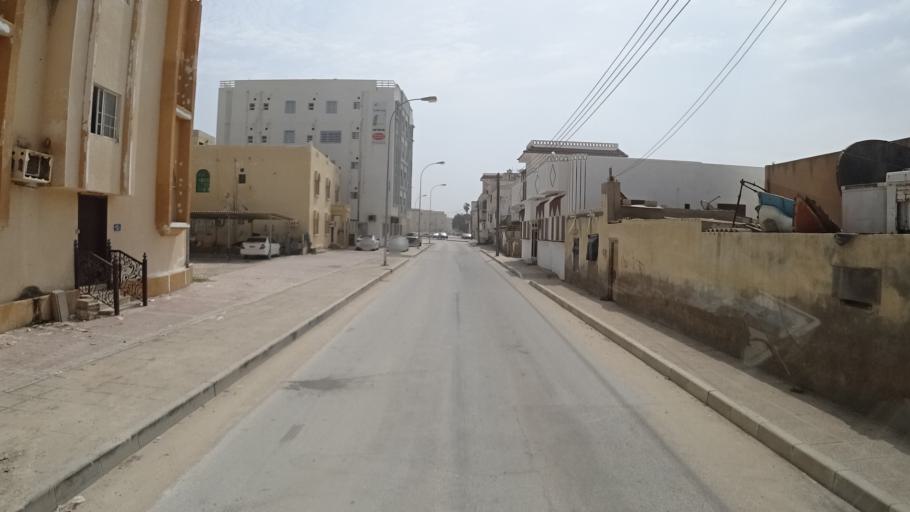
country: OM
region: Zufar
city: Salalah
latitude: 17.0100
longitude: 54.1628
